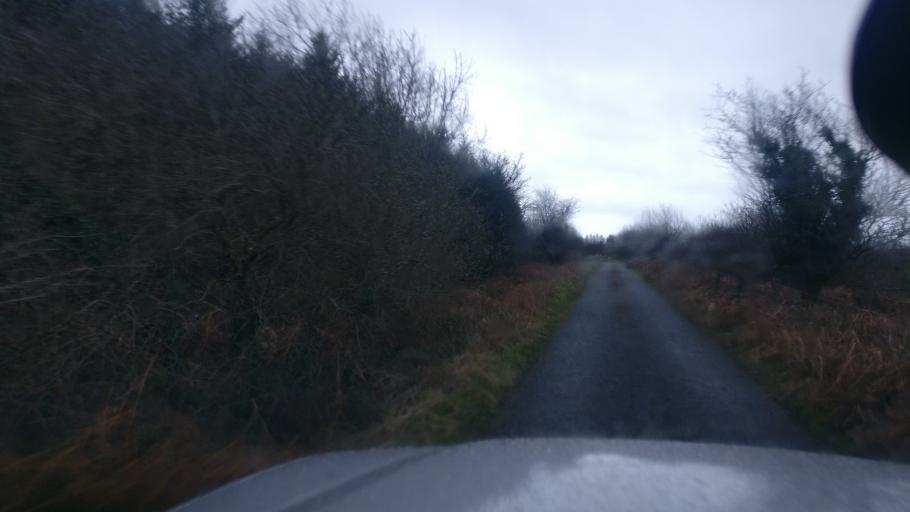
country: IE
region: Connaught
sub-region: County Galway
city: Loughrea
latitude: 53.2482
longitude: -8.4345
